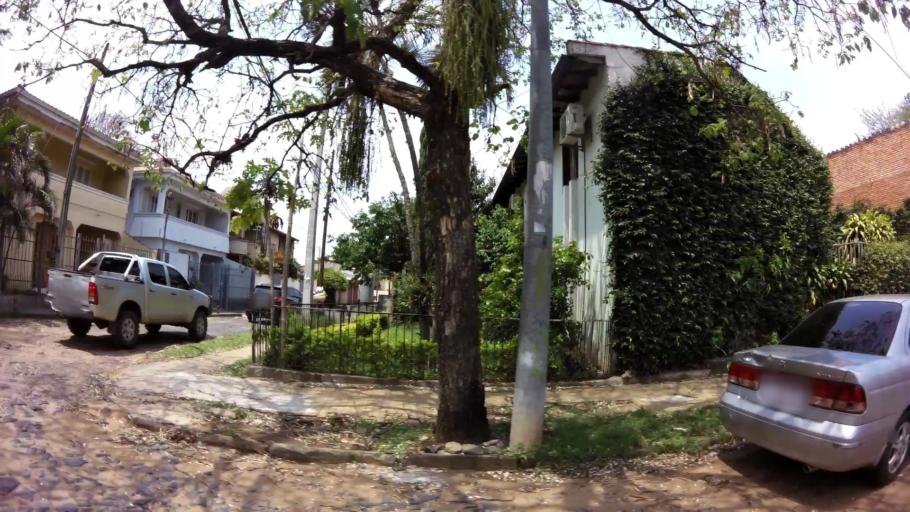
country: PY
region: Asuncion
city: Asuncion
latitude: -25.2711
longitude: -57.5942
